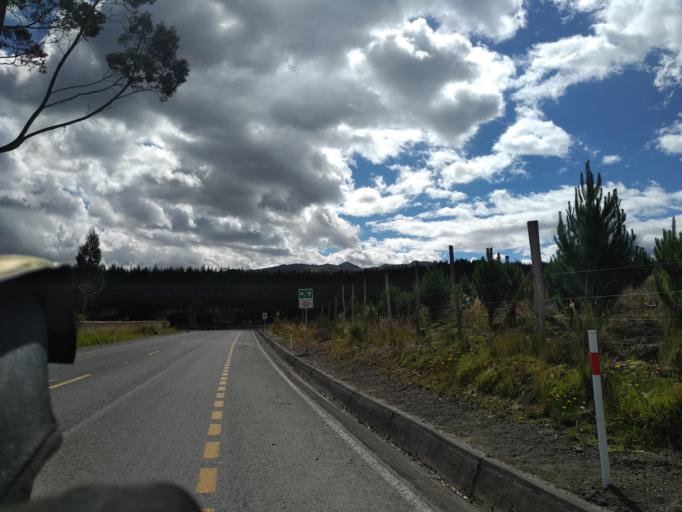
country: EC
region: Cotopaxi
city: Saquisili
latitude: -0.6925
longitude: -78.5668
